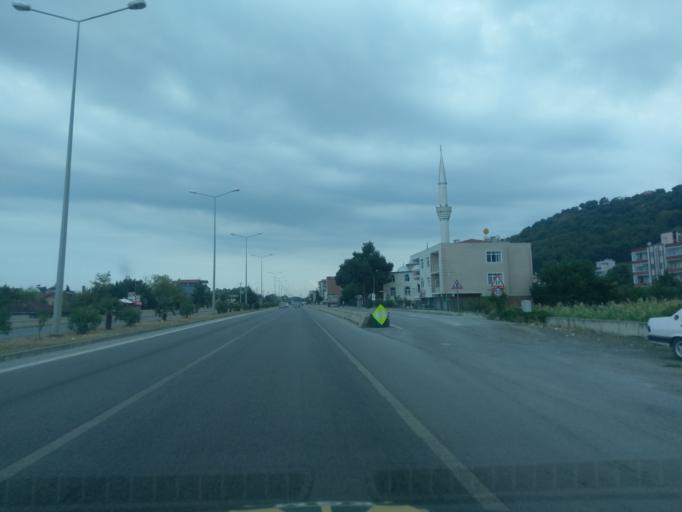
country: TR
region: Samsun
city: Taflan
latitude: 41.3868
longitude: 36.2067
